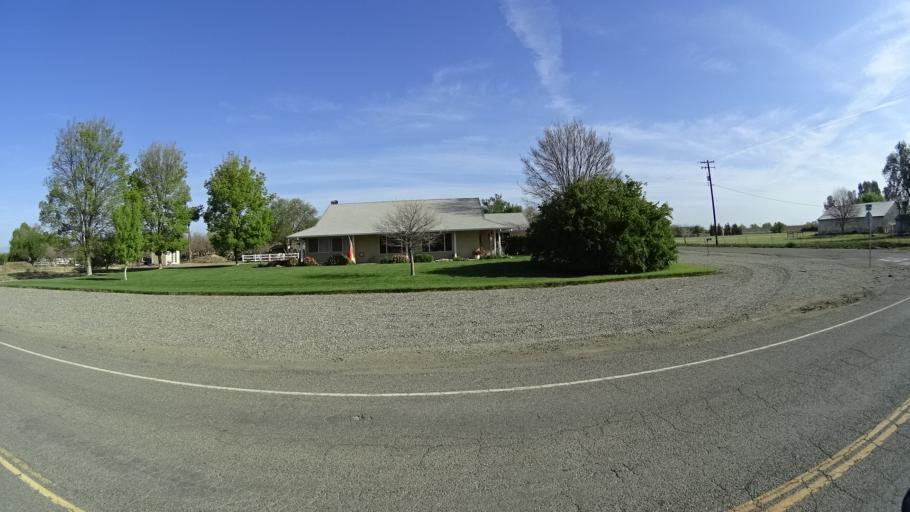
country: US
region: California
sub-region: Glenn County
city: Willows
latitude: 39.5388
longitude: -122.1986
